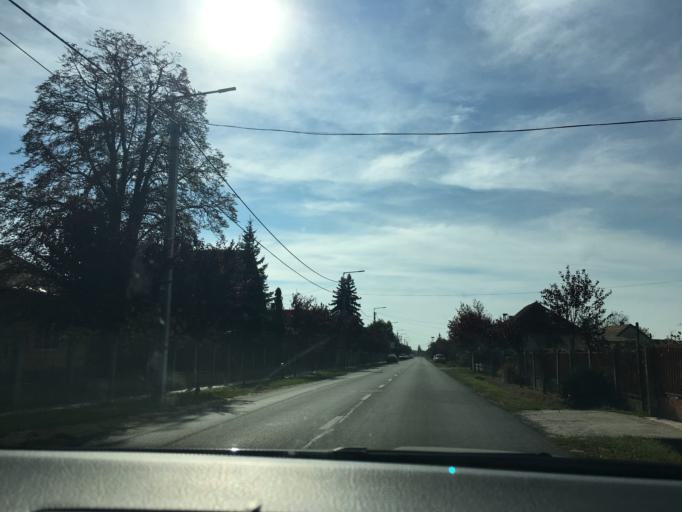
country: HU
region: Hajdu-Bihar
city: Nyirabrany
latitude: 47.5485
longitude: 22.0197
